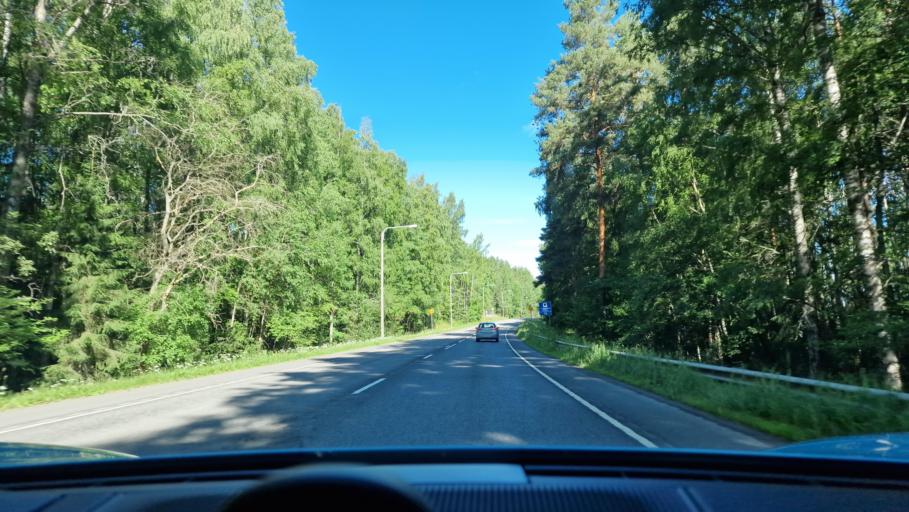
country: FI
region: Pirkanmaa
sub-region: Tampere
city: Kangasala
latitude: 61.4118
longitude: 24.1524
